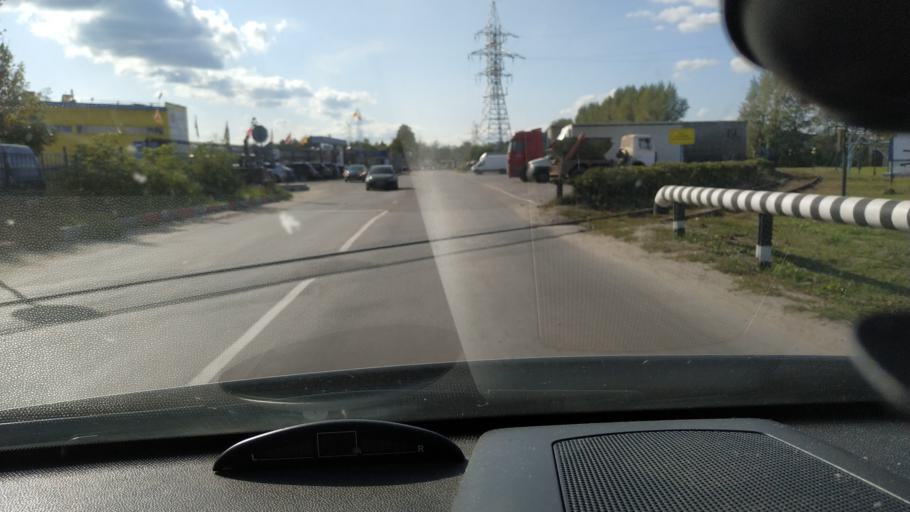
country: RU
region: Rjazan
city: Ryazan'
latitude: 54.6688
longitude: 39.6252
